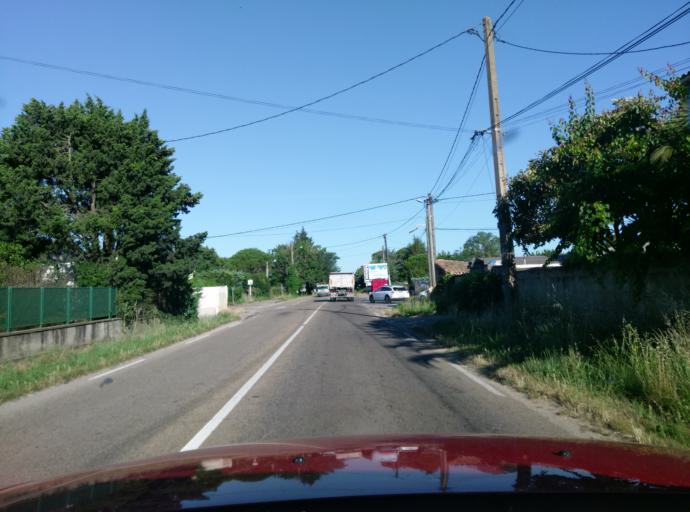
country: FR
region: Languedoc-Roussillon
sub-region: Departement du Gard
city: Redessan
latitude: 43.8268
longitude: 4.4896
